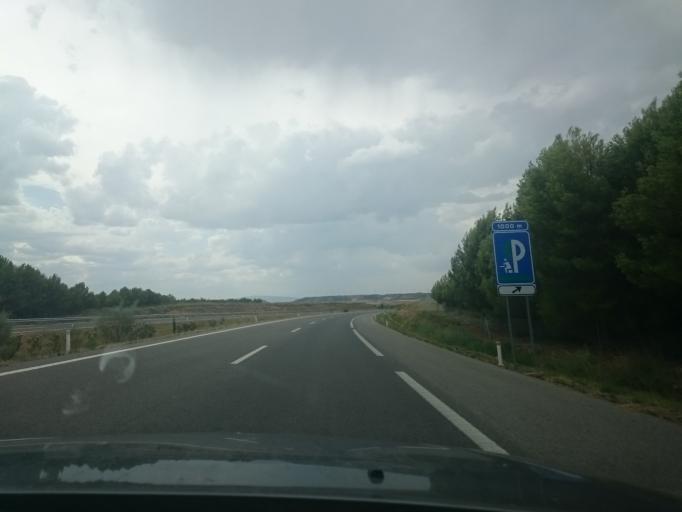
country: ES
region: Navarre
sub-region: Provincia de Navarra
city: Murchante
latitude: 42.0535
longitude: -1.6837
